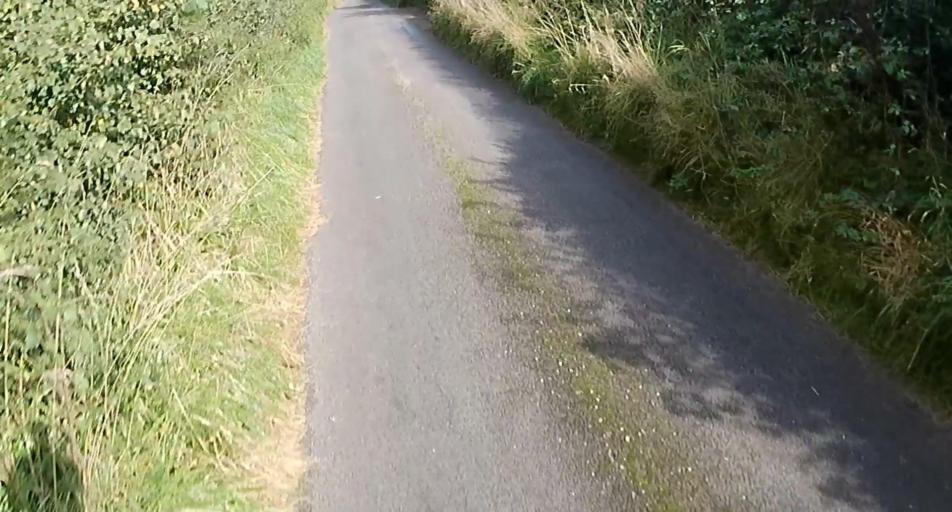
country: GB
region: England
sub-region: Hampshire
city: Tadley
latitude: 51.3093
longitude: -1.1694
